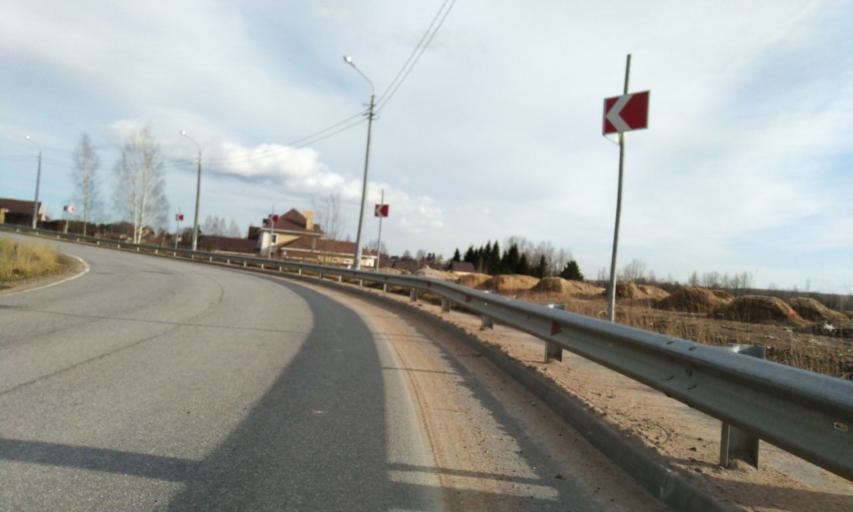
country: RU
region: Leningrad
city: Bugry
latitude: 60.1149
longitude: 30.4240
